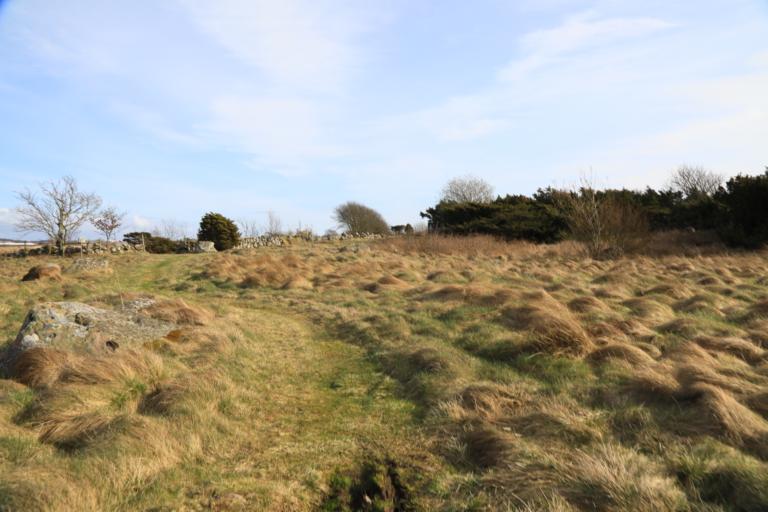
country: SE
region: Halland
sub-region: Varbergs Kommun
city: Varberg
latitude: 57.1276
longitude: 12.2157
